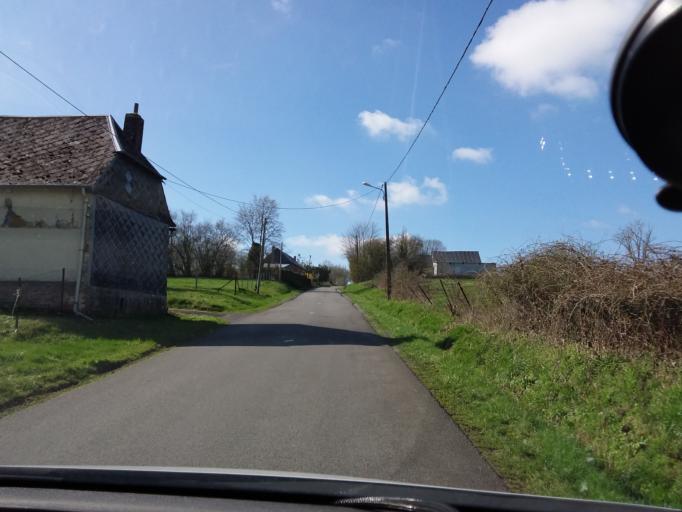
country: FR
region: Picardie
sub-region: Departement de l'Aisne
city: Hirson
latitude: 49.8478
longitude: 4.0769
